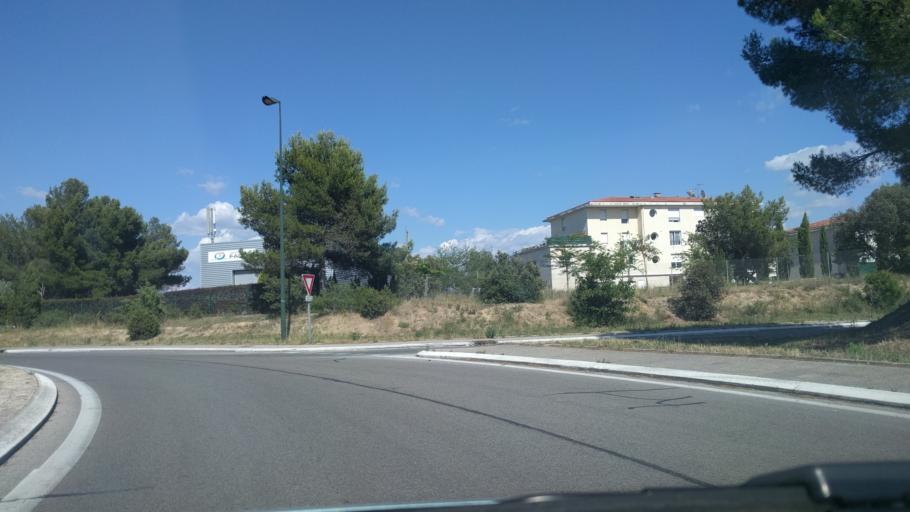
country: FR
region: Provence-Alpes-Cote d'Azur
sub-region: Departement des Bouches-du-Rhone
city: Cabries
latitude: 43.4951
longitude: 5.3504
